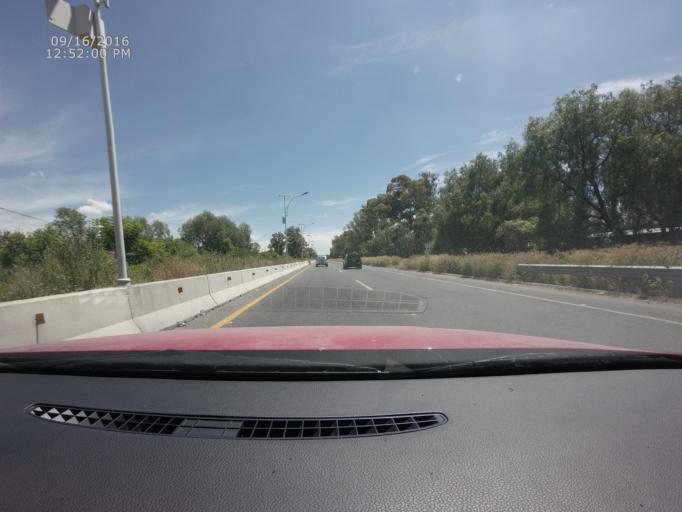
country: MX
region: Queretaro
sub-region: Colon
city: Purisima de Cubos (La Purisima)
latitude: 20.6164
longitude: -100.1493
